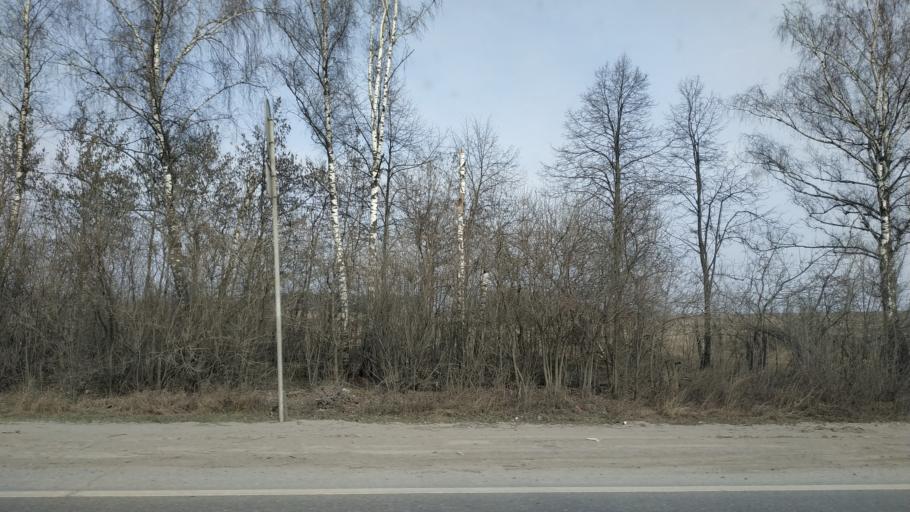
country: RU
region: Moskovskaya
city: Bronnitsy
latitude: 55.3891
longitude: 38.3363
